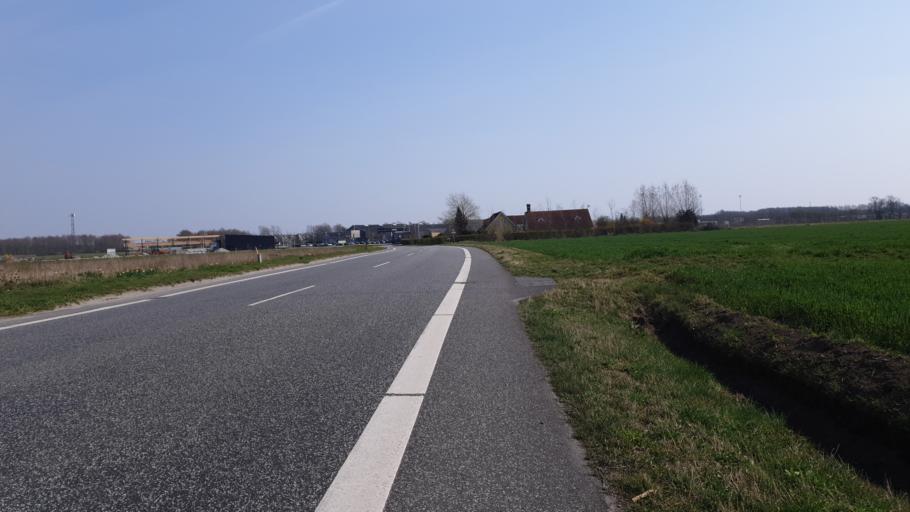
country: DK
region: Central Jutland
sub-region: Hedensted Kommune
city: Hedensted
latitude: 55.7829
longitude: 9.6862
